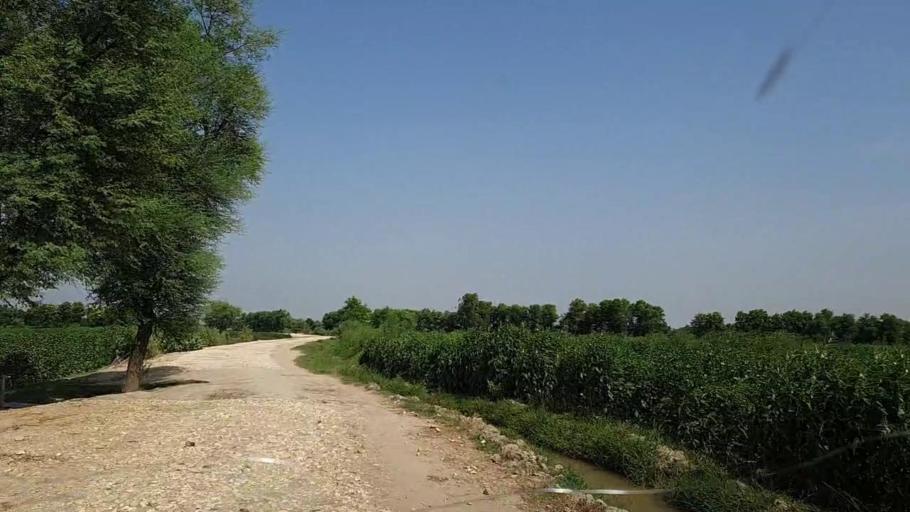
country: PK
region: Sindh
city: Khanpur
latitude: 27.7487
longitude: 69.3473
